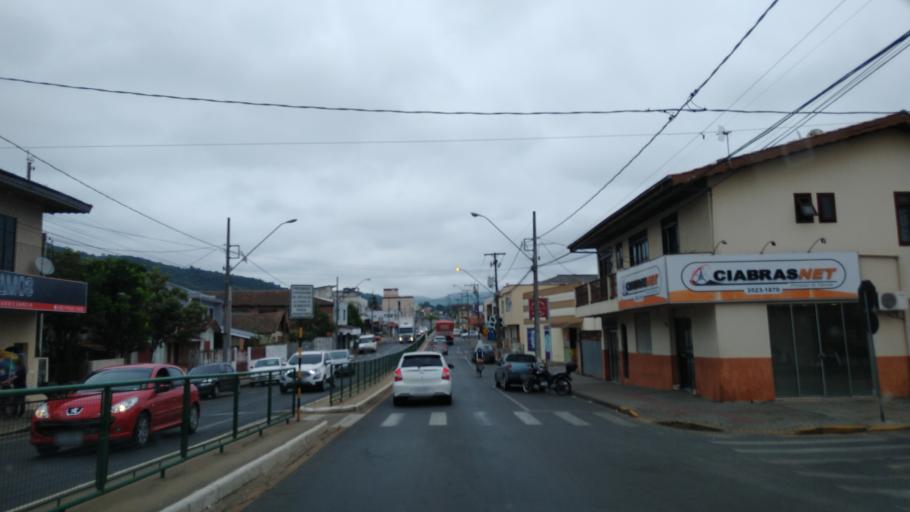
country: BR
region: Santa Catarina
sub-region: Porto Uniao
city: Porto Uniao
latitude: -26.2512
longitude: -51.0853
